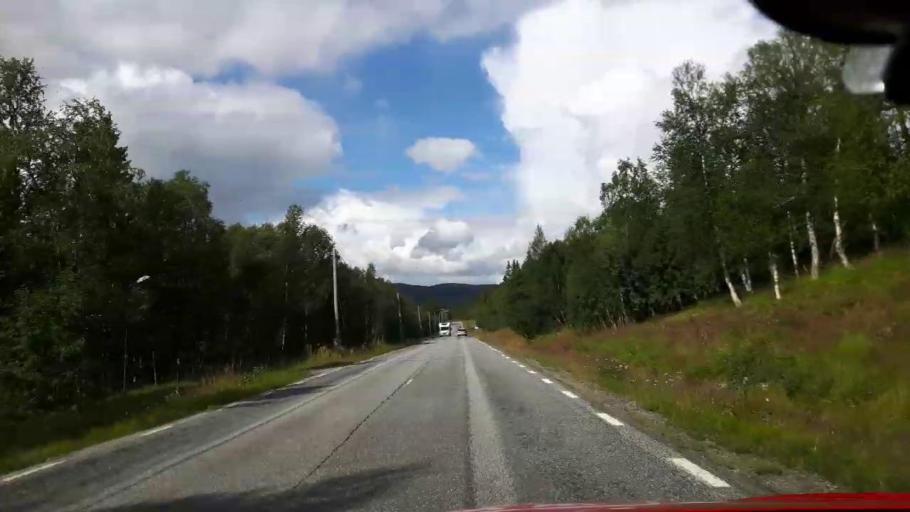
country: NO
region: Nordland
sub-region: Hattfjelldal
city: Hattfjelldal
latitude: 65.0619
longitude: 14.8832
